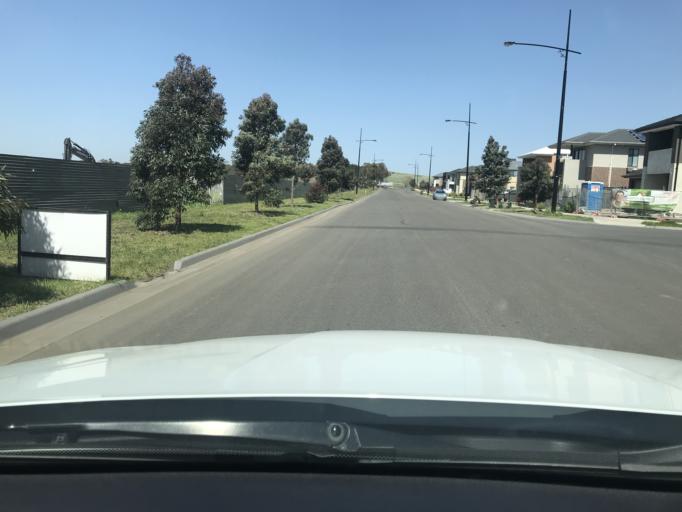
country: AU
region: Victoria
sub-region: Hume
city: Roxburgh Park
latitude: -37.6033
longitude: 144.9038
